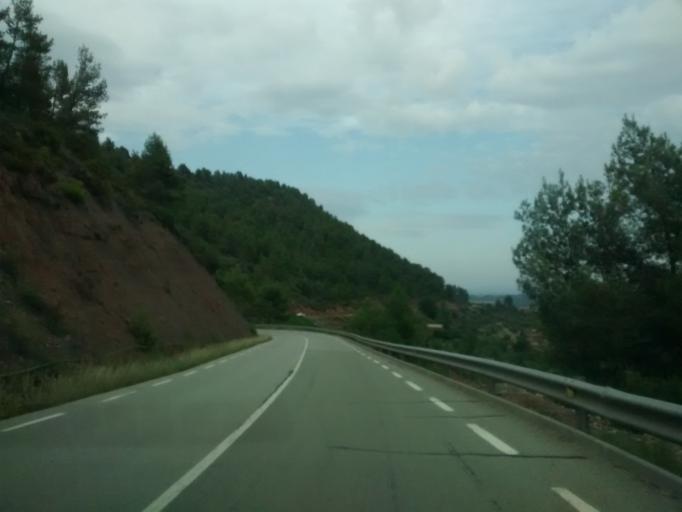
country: ES
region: Catalonia
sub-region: Provincia de Barcelona
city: Fonollosa
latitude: 41.7607
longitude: 1.6898
